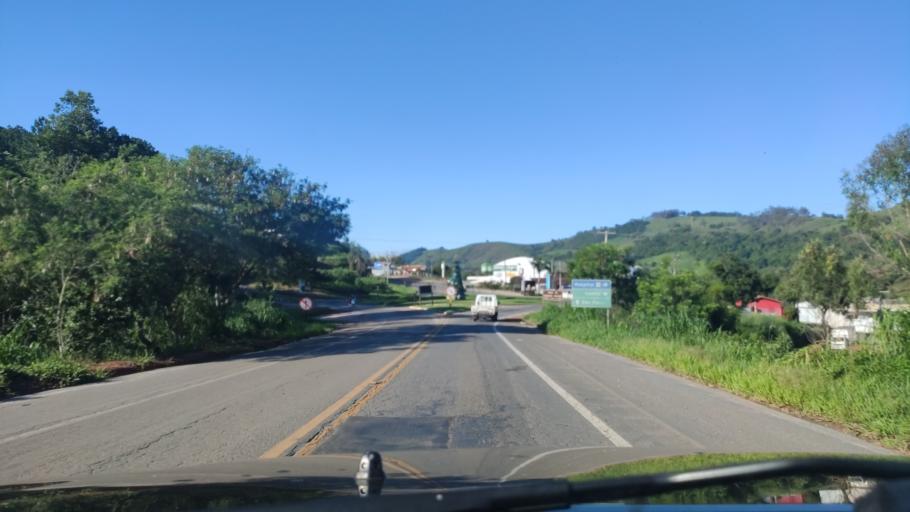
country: BR
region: Sao Paulo
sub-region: Socorro
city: Socorro
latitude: -22.6025
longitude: -46.5238
